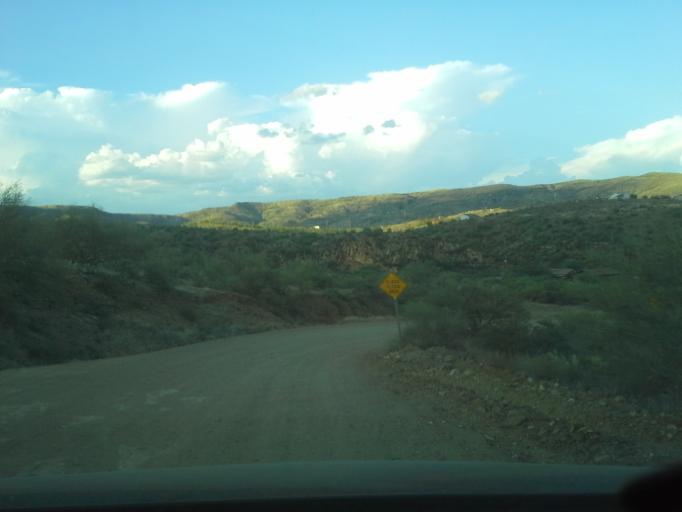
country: US
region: Arizona
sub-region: Yavapai County
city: Spring Valley
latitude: 34.2741
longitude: -112.2045
